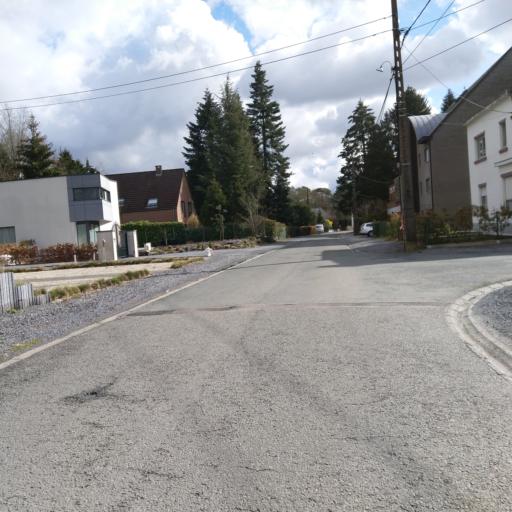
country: BE
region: Wallonia
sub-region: Province du Hainaut
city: Mons
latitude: 50.4921
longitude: 3.9374
